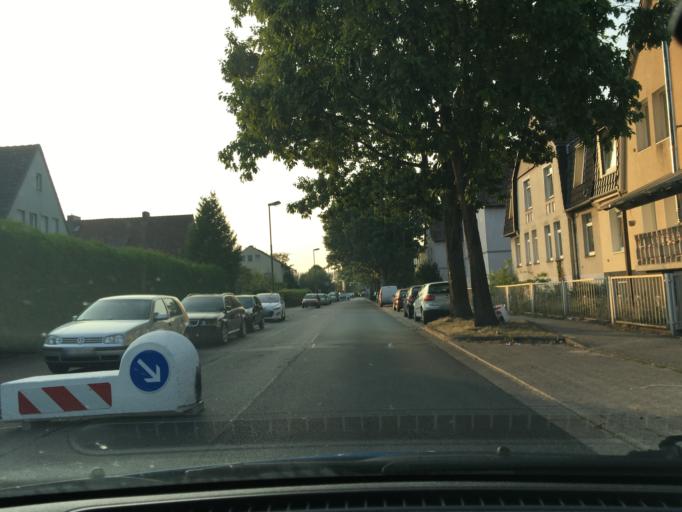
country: DE
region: Lower Saxony
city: Langenhagen
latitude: 52.4517
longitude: 9.7252
